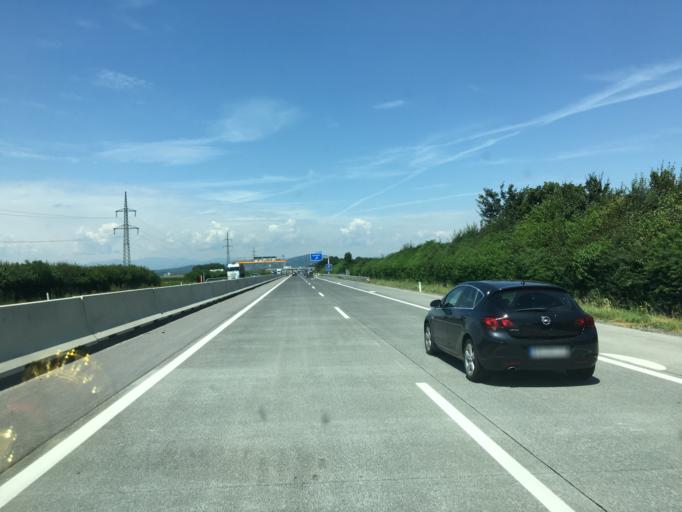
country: AT
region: Styria
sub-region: Politischer Bezirk Graz-Umgebung
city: Zettling
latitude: 46.9576
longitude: 15.4428
